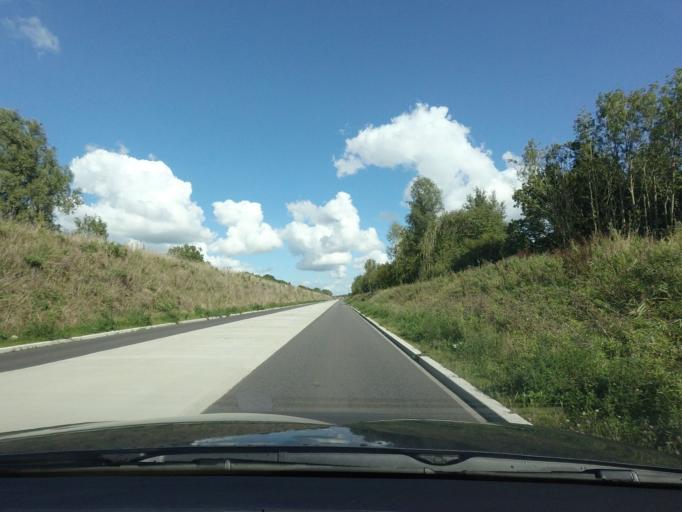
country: NL
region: North Holland
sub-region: Gemeente Heerhugowaard
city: Heerhugowaard
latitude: 52.6586
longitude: 4.8429
